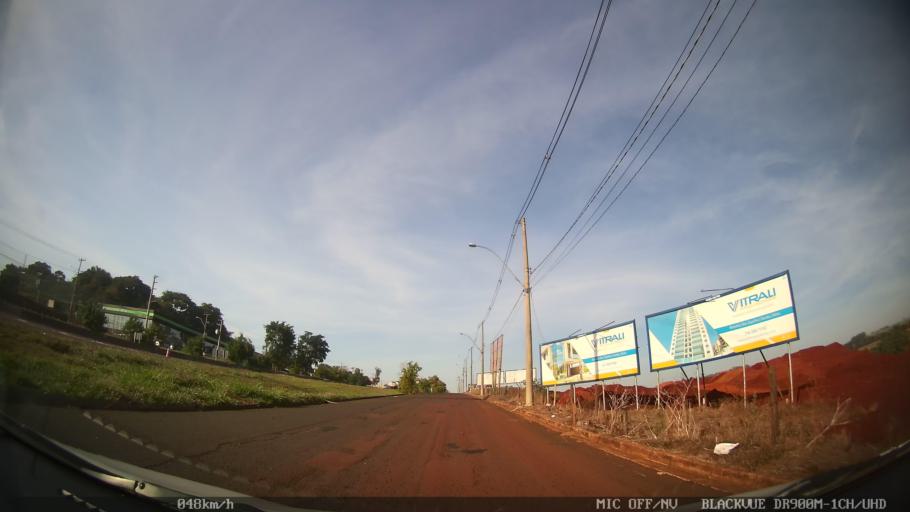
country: BR
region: Sao Paulo
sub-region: Ribeirao Preto
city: Ribeirao Preto
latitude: -21.2505
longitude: -47.8199
